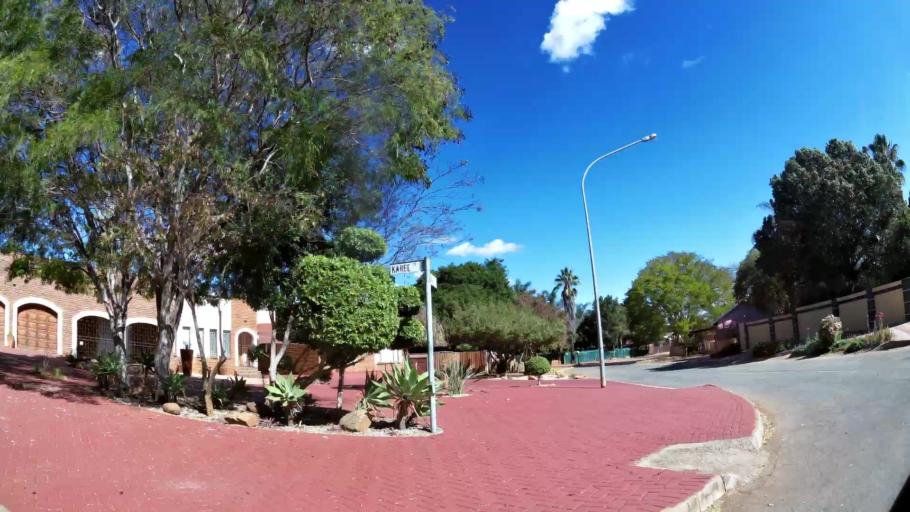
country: ZA
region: Limpopo
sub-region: Capricorn District Municipality
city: Polokwane
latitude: -23.9122
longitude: 29.4922
